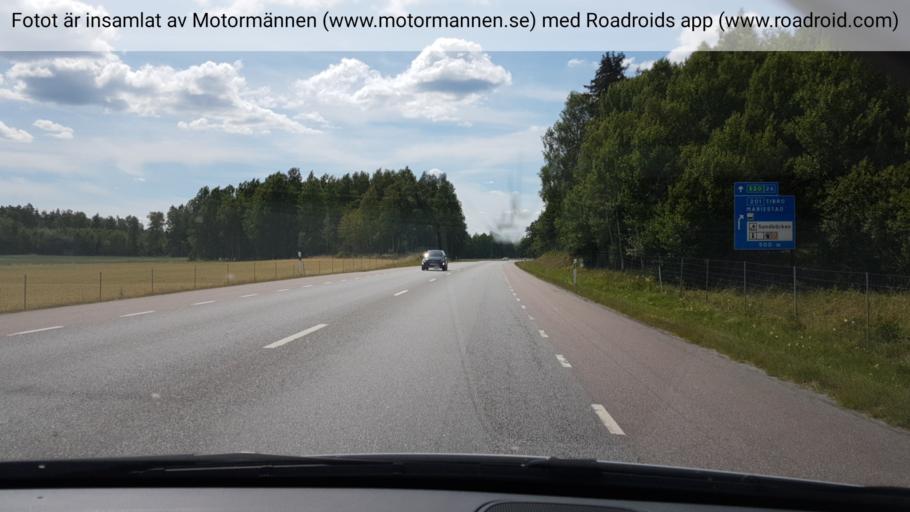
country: SE
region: Vaestra Goetaland
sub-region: Mariestads Kommun
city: Mariestad
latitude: 58.6900
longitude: 13.8578
